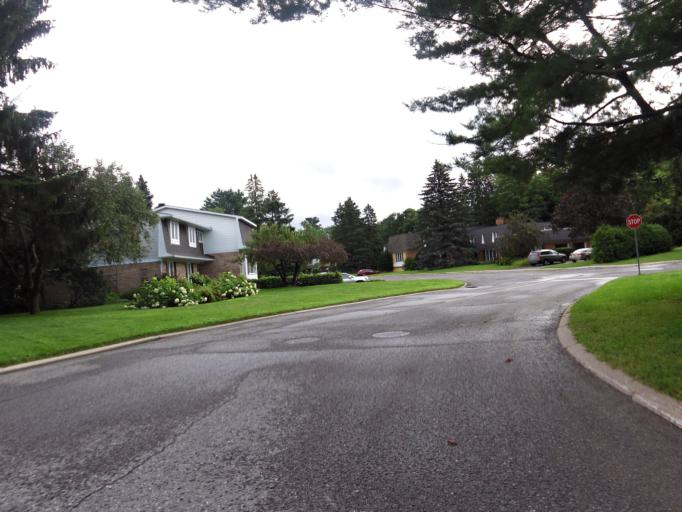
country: CA
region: Ontario
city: Bells Corners
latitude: 45.3214
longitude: -75.7884
